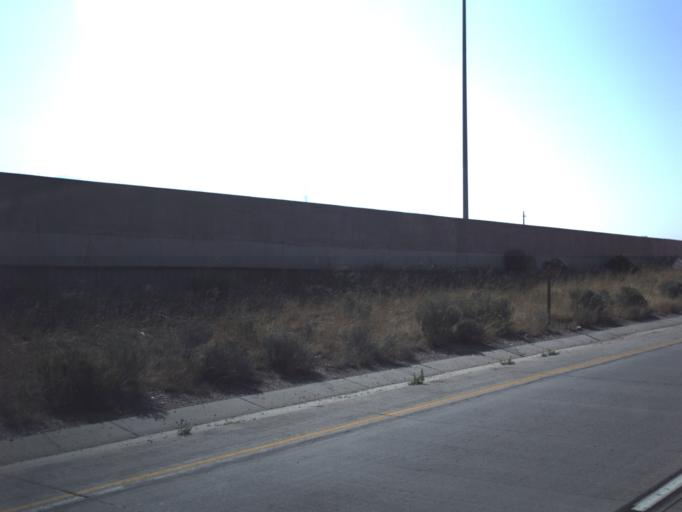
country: US
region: Utah
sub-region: Salt Lake County
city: Murray
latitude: 40.6520
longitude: -111.9025
